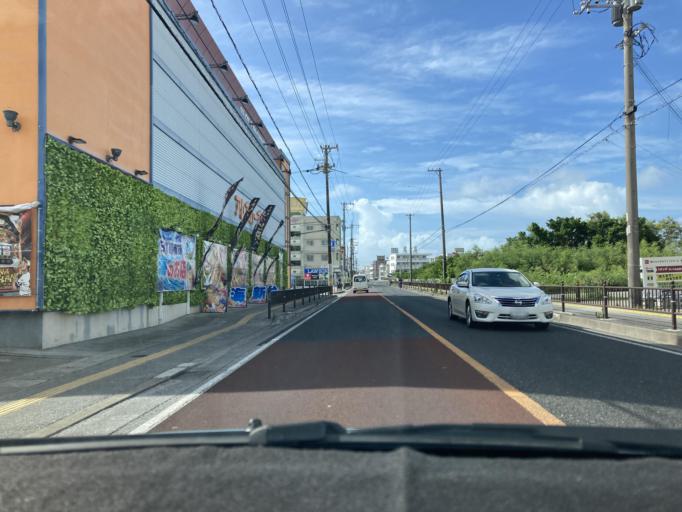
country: JP
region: Okinawa
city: Itoman
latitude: 26.1388
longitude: 127.6710
